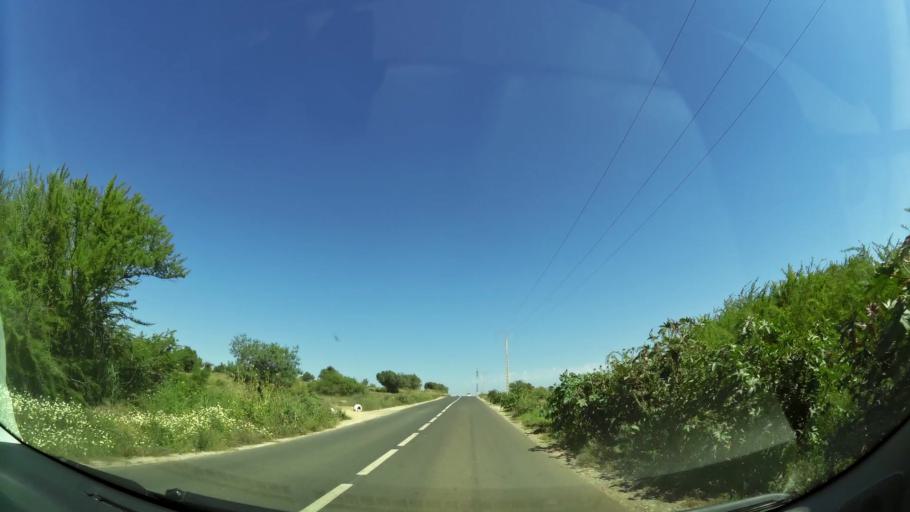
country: MA
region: Oriental
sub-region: Berkane-Taourirt
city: Madagh
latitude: 35.0146
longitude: -2.4022
